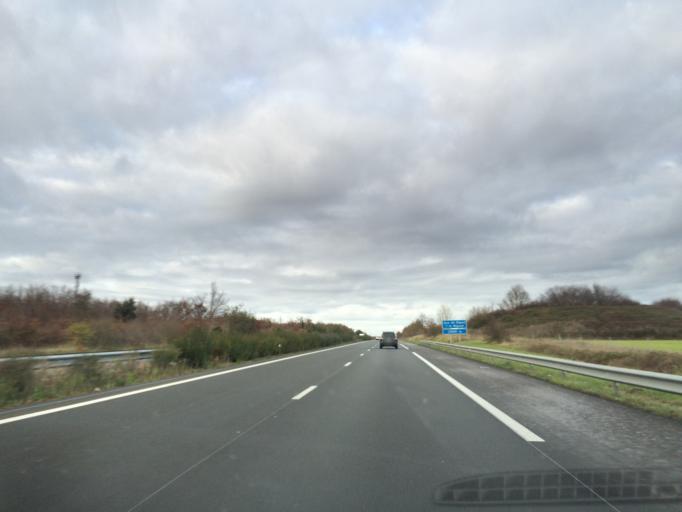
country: FR
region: Poitou-Charentes
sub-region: Departement des Deux-Sevres
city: Beauvoir-sur-Niort
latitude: 46.0891
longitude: -0.5322
